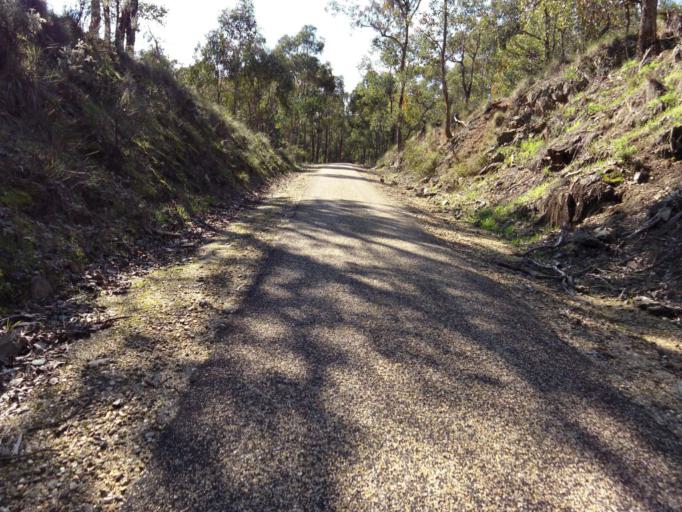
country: AU
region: Victoria
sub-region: Wangaratta
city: Wangaratta
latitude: -36.4061
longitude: 146.6210
